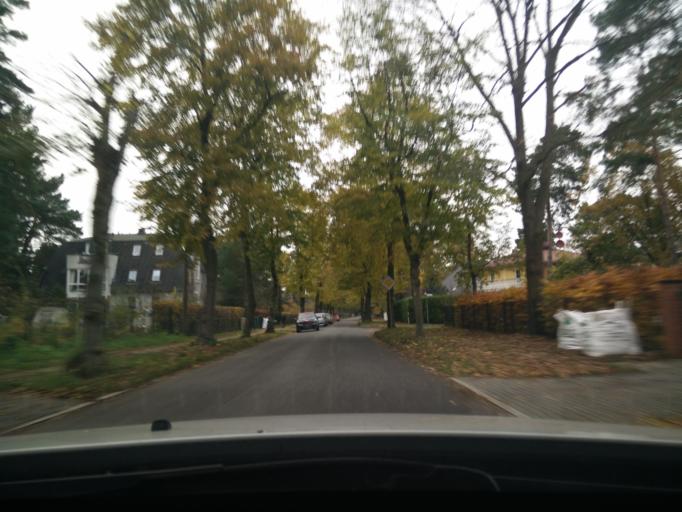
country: DE
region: Brandenburg
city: Falkensee
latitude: 52.5723
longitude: 13.1292
